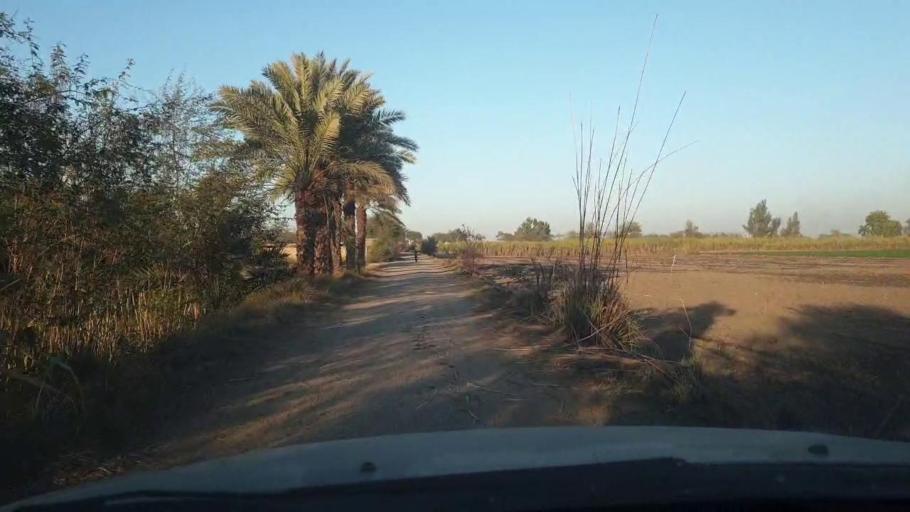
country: PK
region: Sindh
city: Ghotki
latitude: 28.0327
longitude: 69.2952
